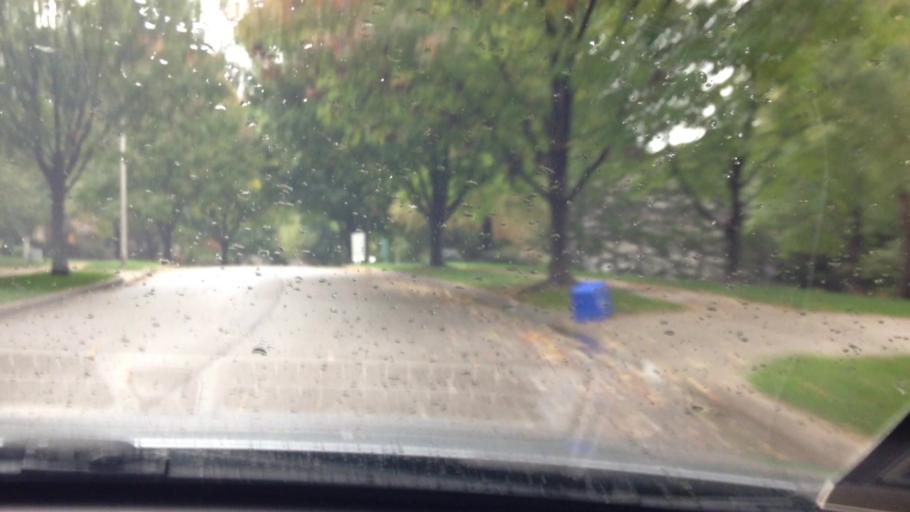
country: US
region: Missouri
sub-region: Platte County
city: Riverside
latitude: 39.1758
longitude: -94.5965
